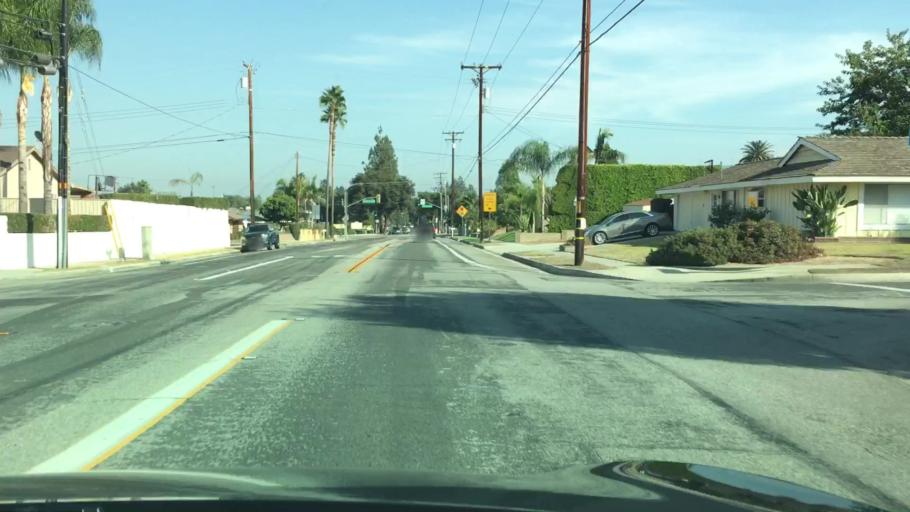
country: US
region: California
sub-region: Los Angeles County
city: Hacienda Heights
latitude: 34.0089
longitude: -117.9815
